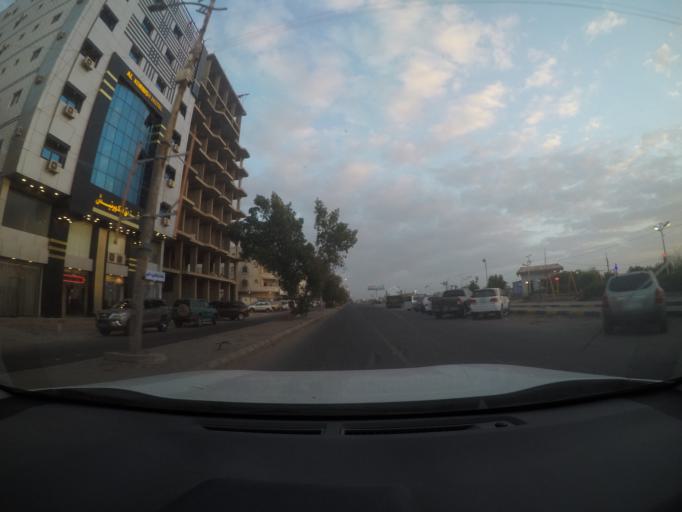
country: YE
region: Aden
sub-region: Khur Maksar
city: Khawr Maksar
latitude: 12.8414
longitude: 45.0516
